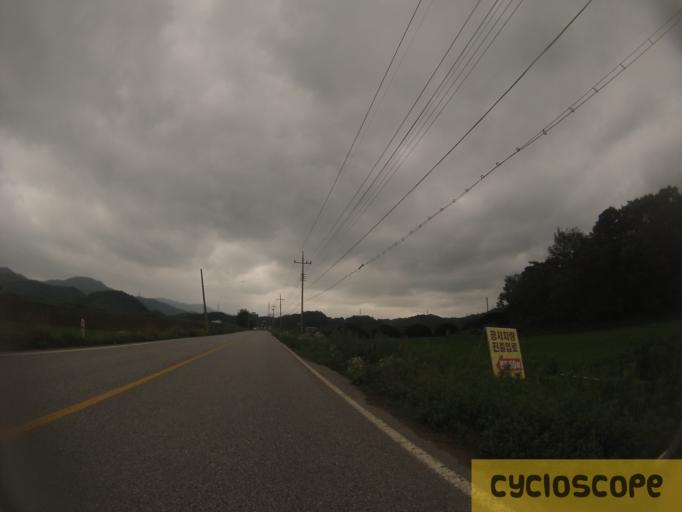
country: KR
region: Chungcheongnam-do
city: Yesan
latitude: 36.5930
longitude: 126.7935
